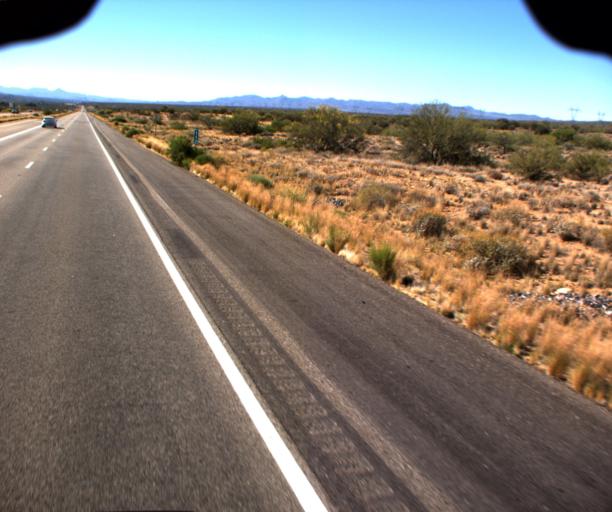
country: US
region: Arizona
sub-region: Mohave County
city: Kingman
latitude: 34.8703
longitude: -113.6448
